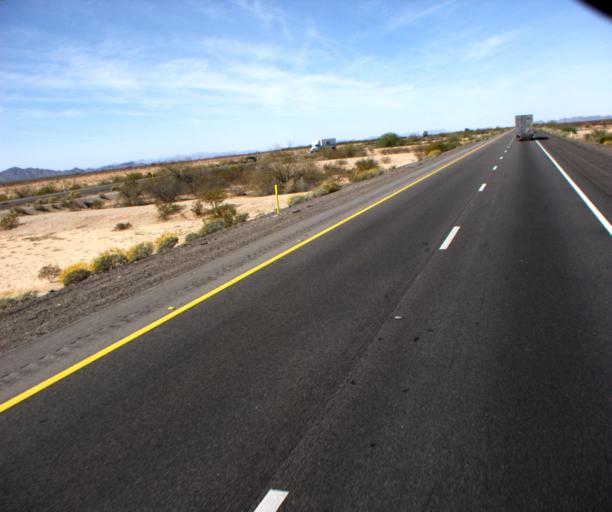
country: US
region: Arizona
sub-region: La Paz County
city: Salome
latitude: 33.5780
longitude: -113.4106
